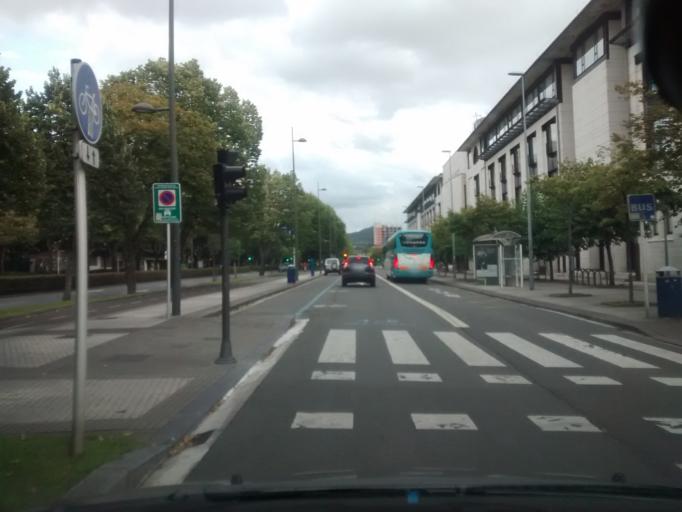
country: ES
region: Basque Country
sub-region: Provincia de Guipuzcoa
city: San Sebastian
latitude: 43.3081
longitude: -2.0097
